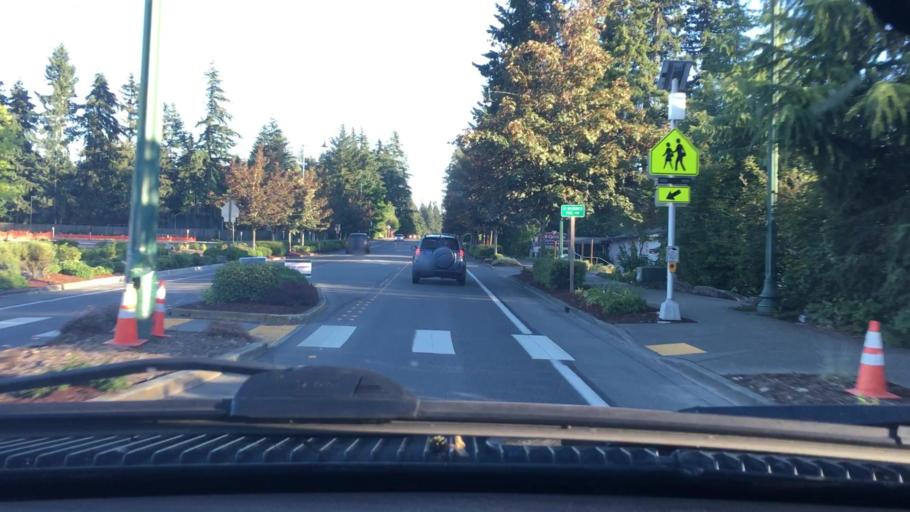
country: US
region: Washington
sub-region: King County
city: Maple Valley
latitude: 47.3848
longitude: -122.0482
